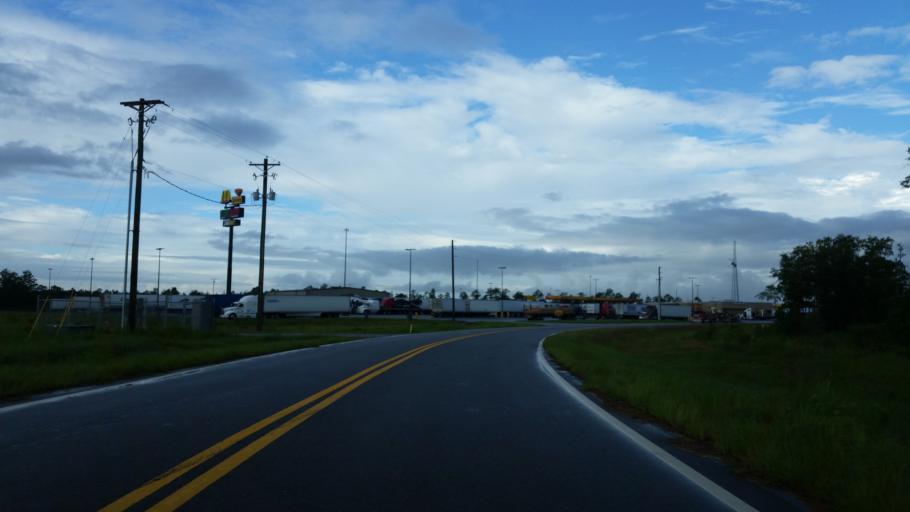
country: US
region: Florida
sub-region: Okaloosa County
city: Crestview
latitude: 30.7355
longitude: -86.3459
